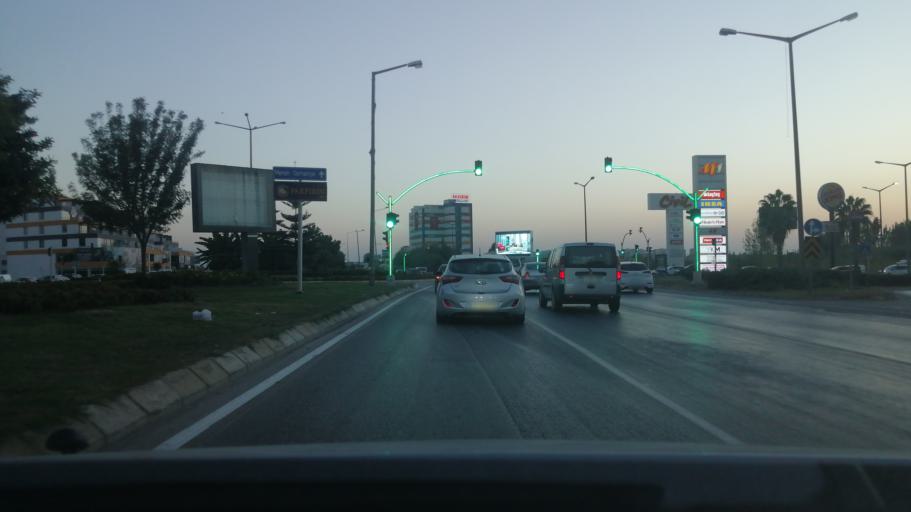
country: TR
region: Adana
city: Seyhan
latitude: 37.0162
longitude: 35.2510
